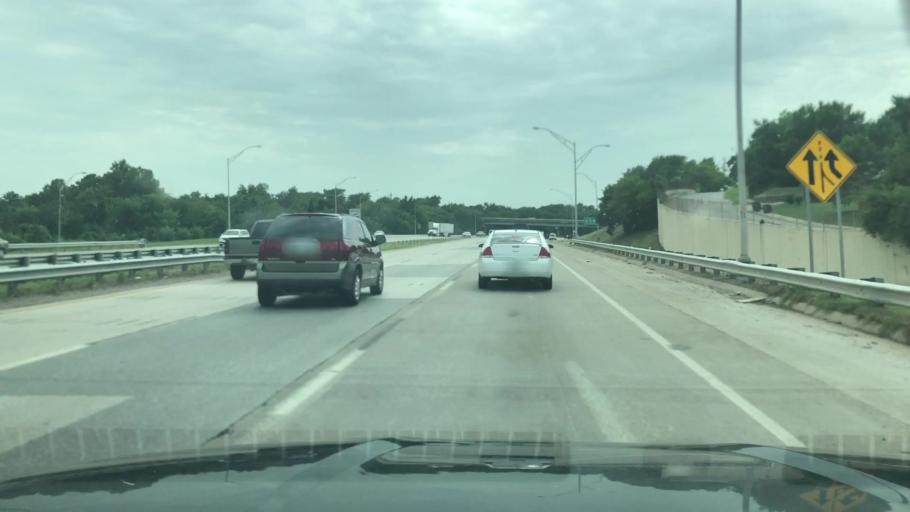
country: US
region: Oklahoma
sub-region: Tulsa County
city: Tulsa
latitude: 36.1564
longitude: -96.0077
